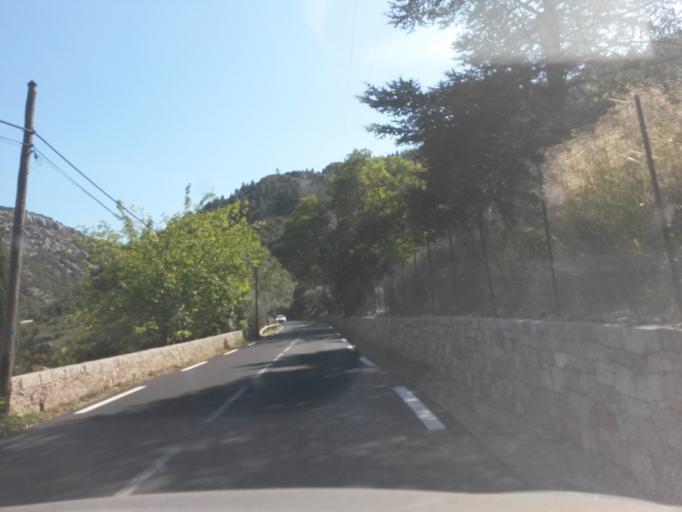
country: FR
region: Languedoc-Roussillon
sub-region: Departement de l'Herault
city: Saint-Jean-de-Fos
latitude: 43.7265
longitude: 3.5500
